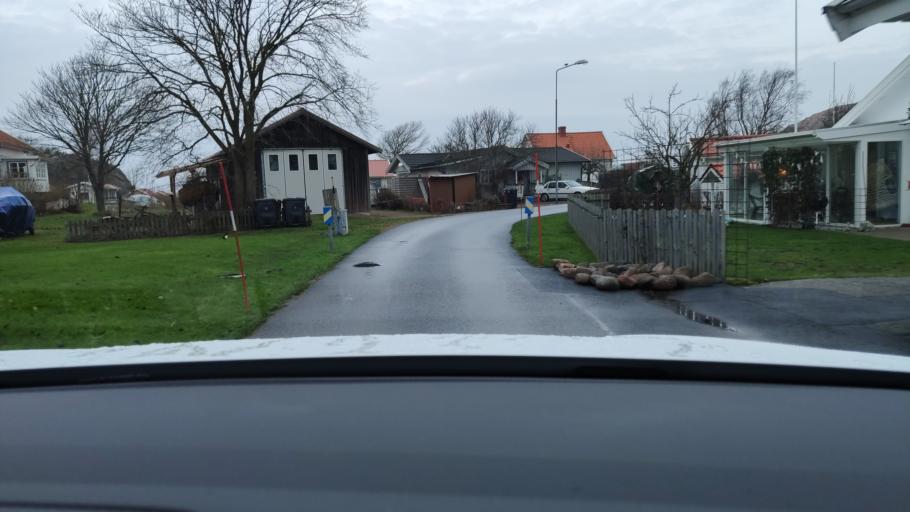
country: SE
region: Vaestra Goetaland
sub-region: Lysekils Kommun
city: Lysekil
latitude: 58.3215
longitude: 11.4045
